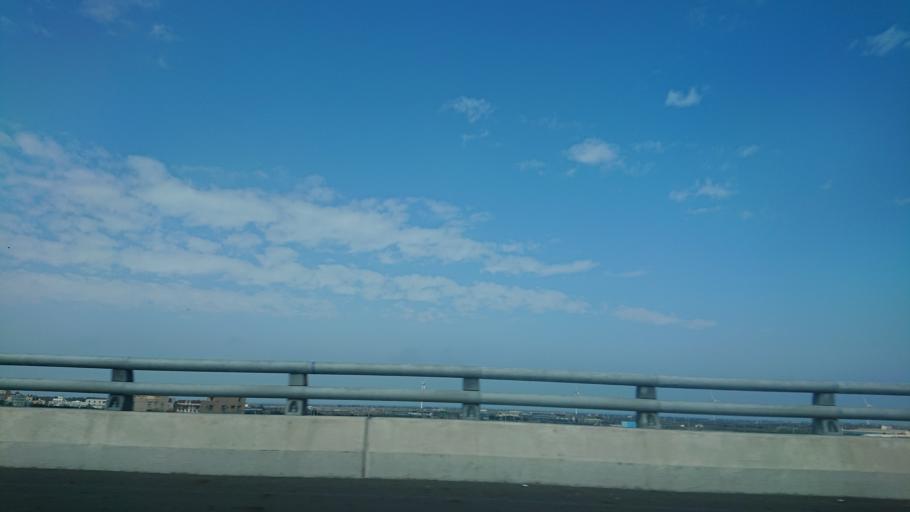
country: TW
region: Taiwan
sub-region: Changhua
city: Chang-hua
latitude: 23.9669
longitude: 120.3398
